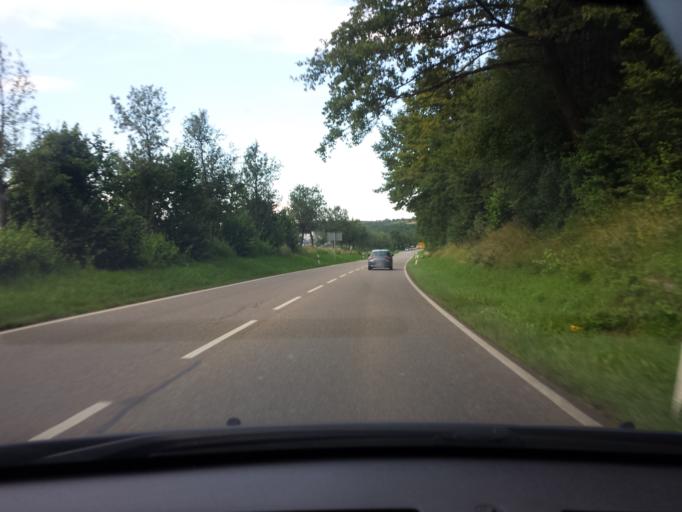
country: DE
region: Baden-Wuerttemberg
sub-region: Regierungsbezirk Stuttgart
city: Stuttgart Muehlhausen
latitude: 48.8682
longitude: 9.2670
